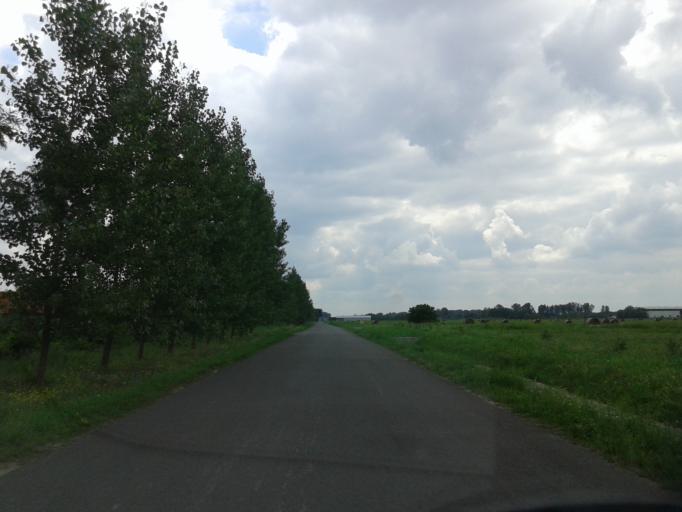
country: HU
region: Csongrad
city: Morahalom
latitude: 46.2139
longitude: 19.8972
